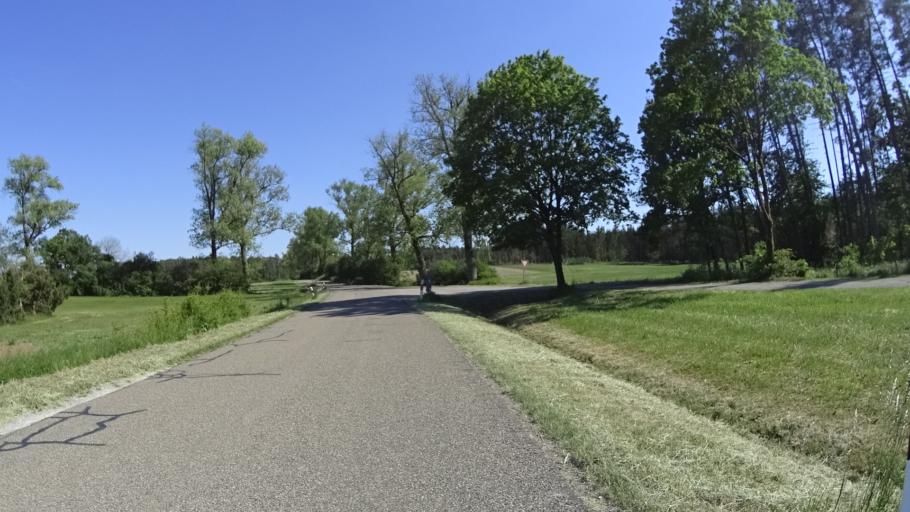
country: DE
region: Bavaria
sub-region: Regierungsbezirk Mittelfranken
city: Dombuhl
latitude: 49.2385
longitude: 10.2902
